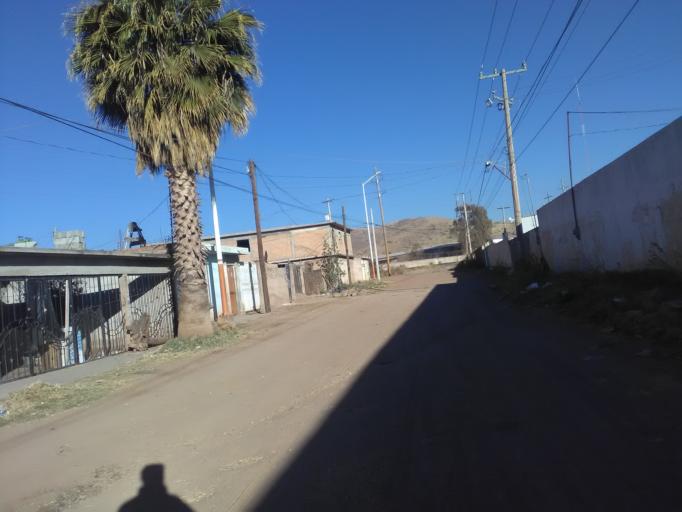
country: MX
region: Durango
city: Victoria de Durango
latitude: 24.0561
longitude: -104.6543
